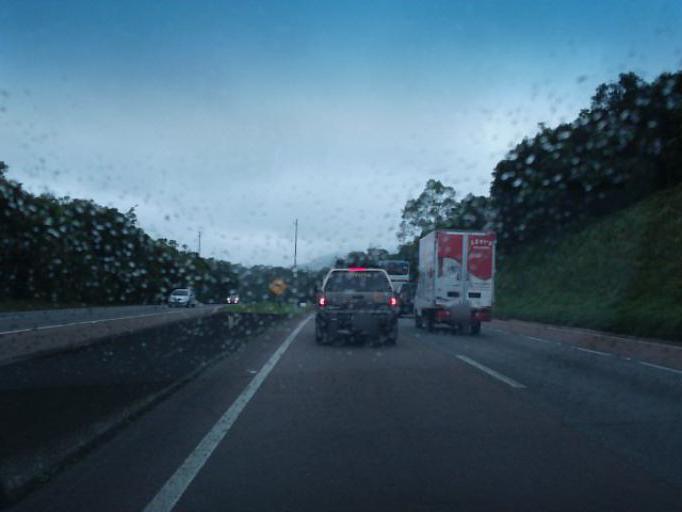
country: BR
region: Parana
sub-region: Sao Jose Dos Pinhais
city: Sao Jose dos Pinhais
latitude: -25.7870
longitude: -49.1230
